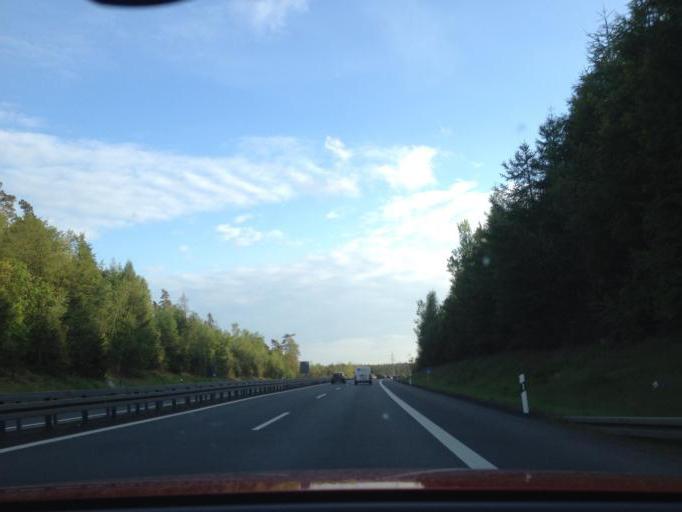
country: DE
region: Bavaria
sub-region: Upper Palatinate
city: Wiesau
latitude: 49.8948
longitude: 12.2193
